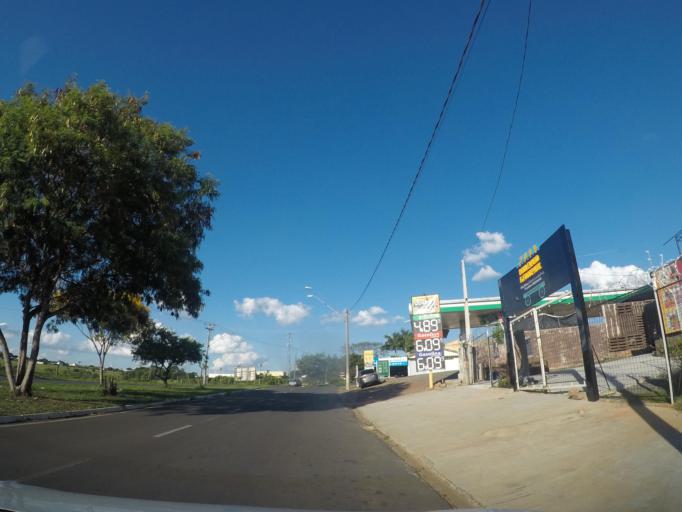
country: BR
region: Sao Paulo
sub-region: Sumare
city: Sumare
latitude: -22.8080
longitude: -47.2274
